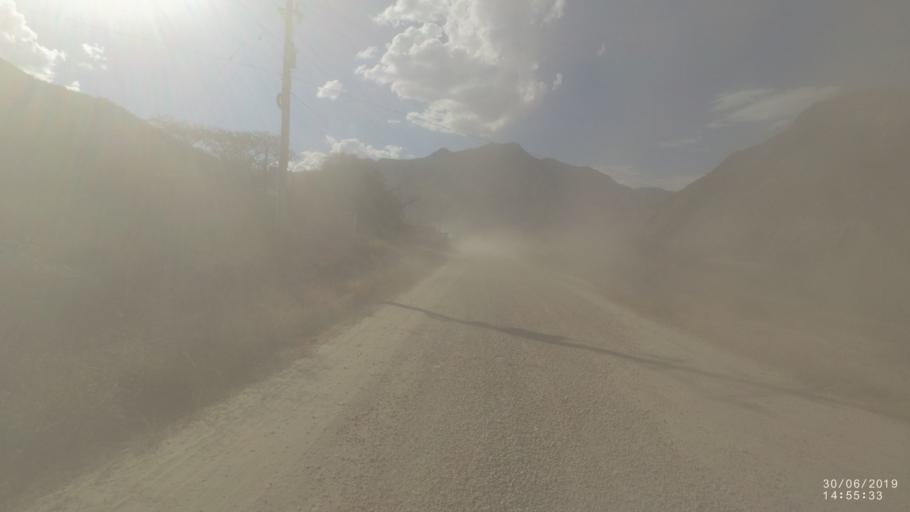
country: BO
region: Cochabamba
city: Irpa Irpa
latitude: -17.7536
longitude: -66.3526
